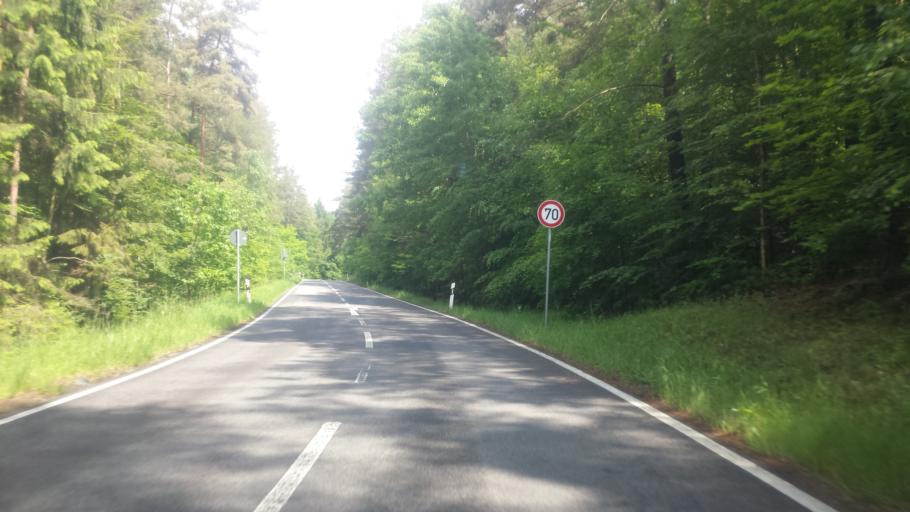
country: DE
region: Rheinland-Pfalz
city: Lindenberg
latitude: 49.4049
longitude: 8.1045
